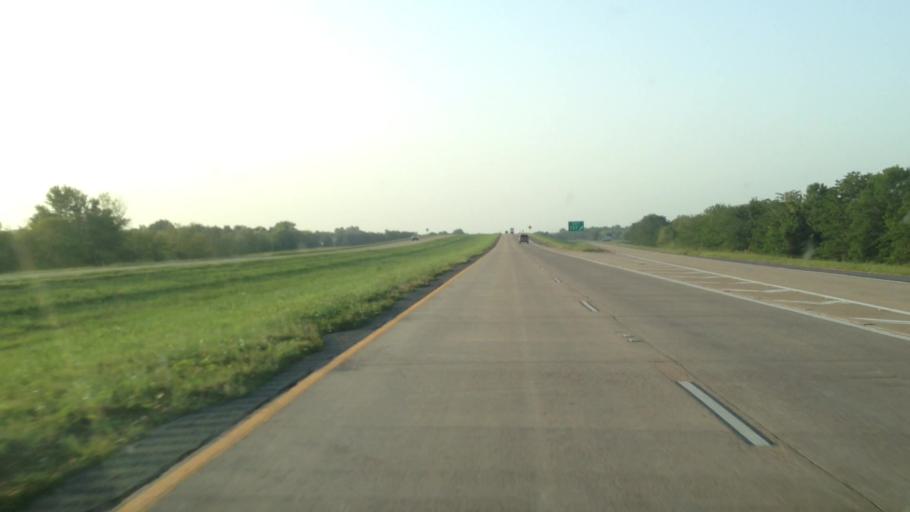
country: US
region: Louisiana
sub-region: Natchitoches Parish
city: Vienna Bend
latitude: 31.6142
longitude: -93.0545
